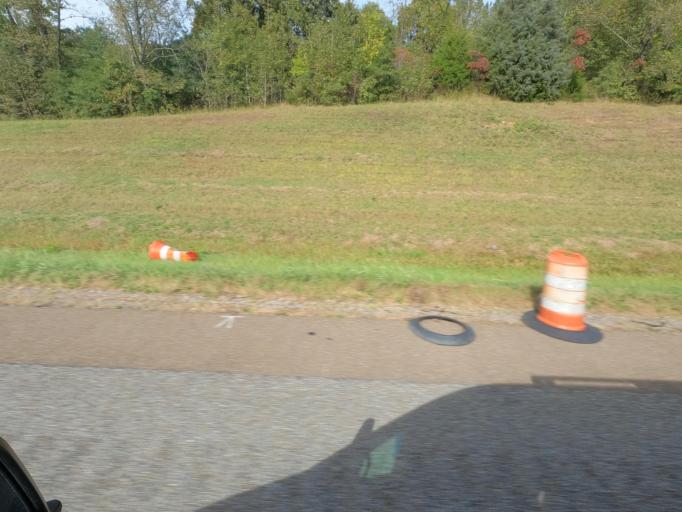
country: US
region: Tennessee
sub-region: Decatur County
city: Parsons
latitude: 35.8432
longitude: -88.0814
